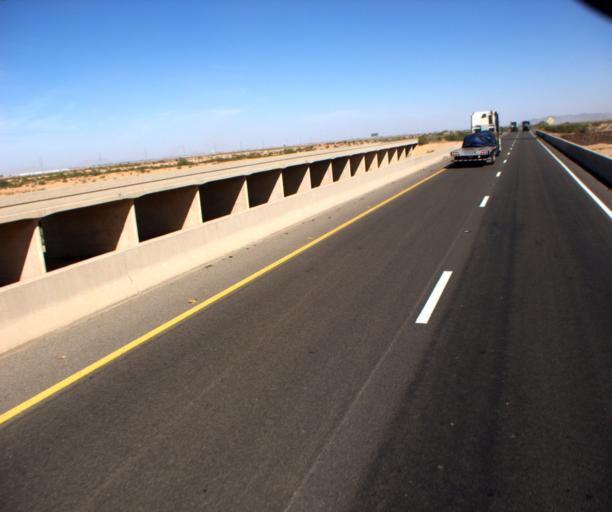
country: US
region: Arizona
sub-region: Pinal County
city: Casa Grande
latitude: 32.8281
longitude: -111.9381
